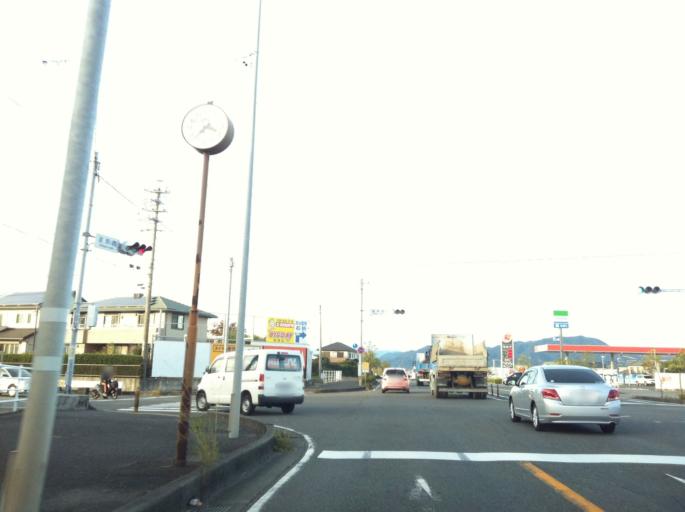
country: JP
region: Shizuoka
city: Yaizu
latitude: 34.8363
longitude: 138.3004
